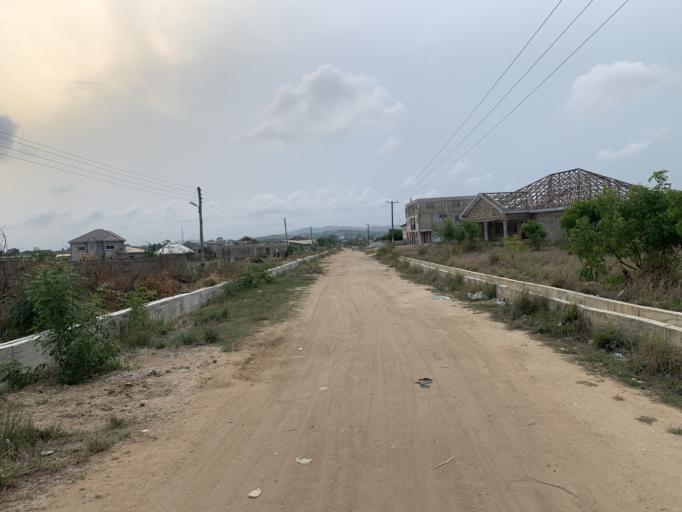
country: GH
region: Central
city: Winneba
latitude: 5.3830
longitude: -0.6279
